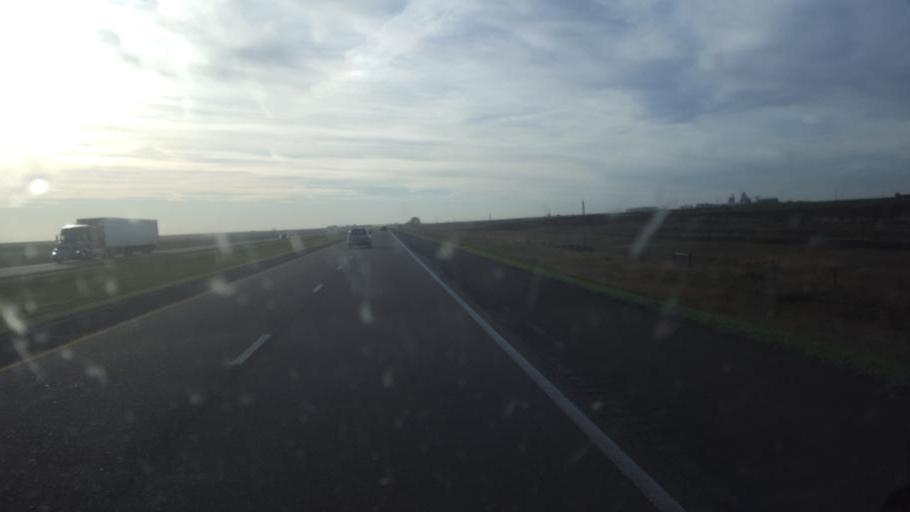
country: US
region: Kansas
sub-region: Logan County
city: Oakley
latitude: 39.1123
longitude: -100.7103
